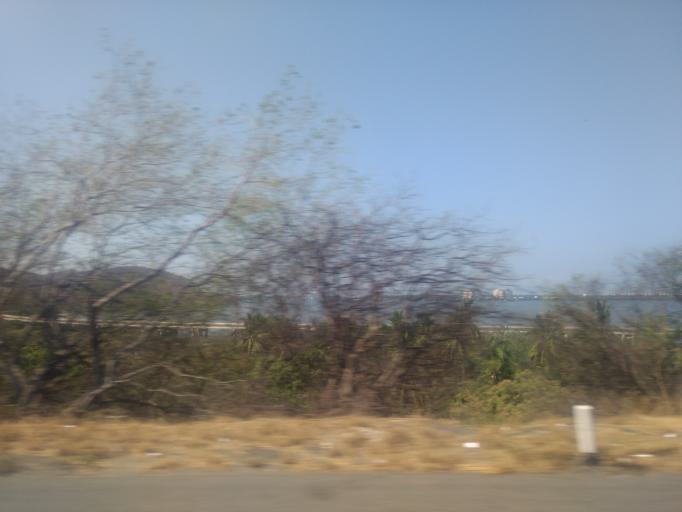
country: MX
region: Colima
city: El Colomo
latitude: 19.0321
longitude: -104.2500
